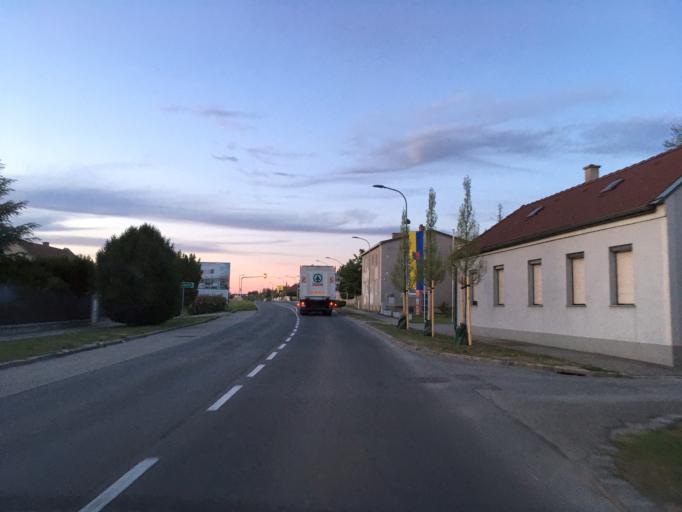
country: AT
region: Lower Austria
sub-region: Politischer Bezirk Wien-Umgebung
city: Zwolfaxing
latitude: 48.1128
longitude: 16.4643
